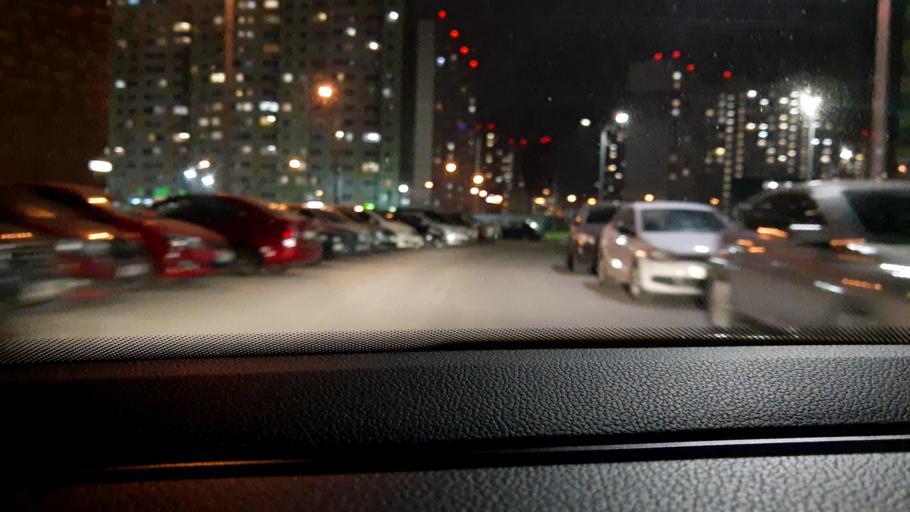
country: RU
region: Moskovskaya
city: Dolgoprudnyy
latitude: 55.9342
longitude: 37.5025
